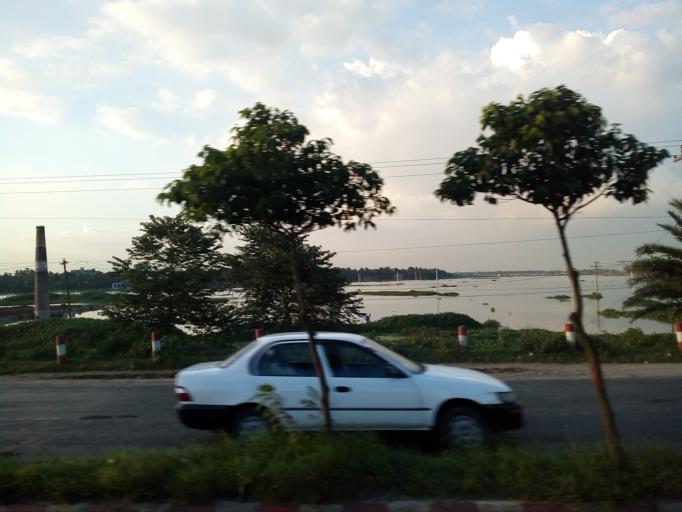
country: BD
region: Dhaka
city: Azimpur
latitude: 23.7945
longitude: 90.2937
